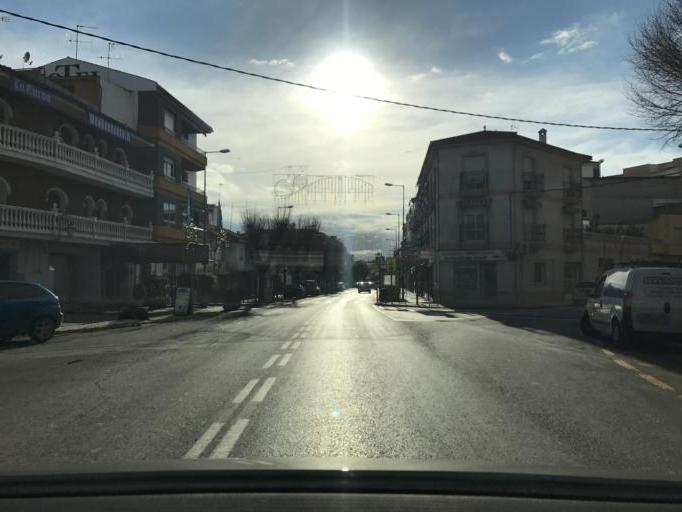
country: ES
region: Andalusia
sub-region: Provincia de Granada
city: Albolote
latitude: 37.2312
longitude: -3.6516
